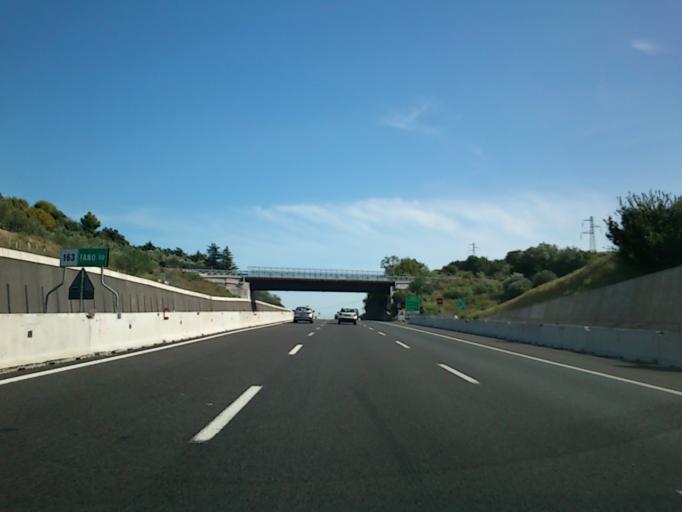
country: IT
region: The Marches
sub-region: Provincia di Pesaro e Urbino
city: Pesaro
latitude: 43.8719
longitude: 12.9189
